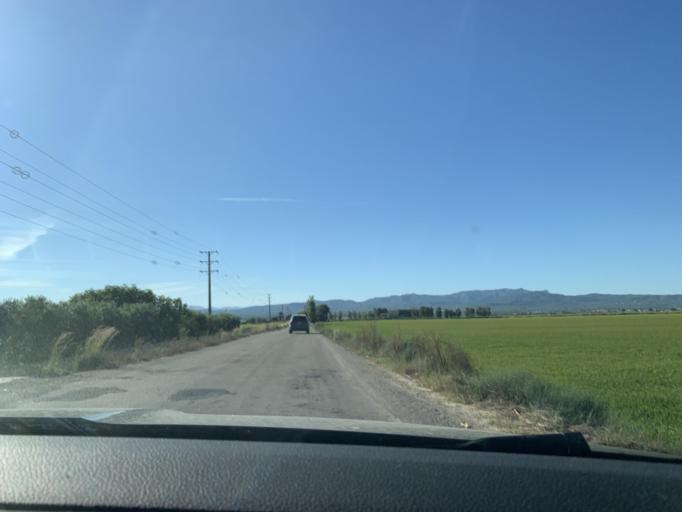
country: ES
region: Catalonia
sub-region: Provincia de Tarragona
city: Deltebre
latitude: 40.7532
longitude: 0.7195
